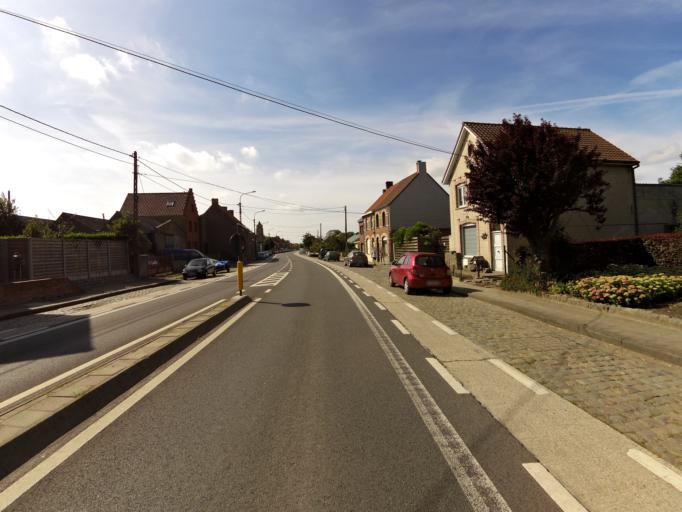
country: BE
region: Flanders
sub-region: Provincie West-Vlaanderen
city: Diksmuide
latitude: 51.0054
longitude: 2.8694
